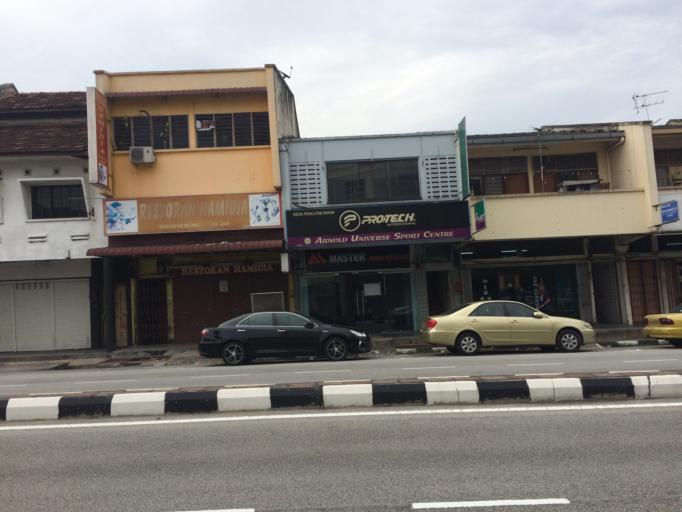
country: MY
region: Perak
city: Ipoh
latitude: 4.6063
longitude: 101.0942
